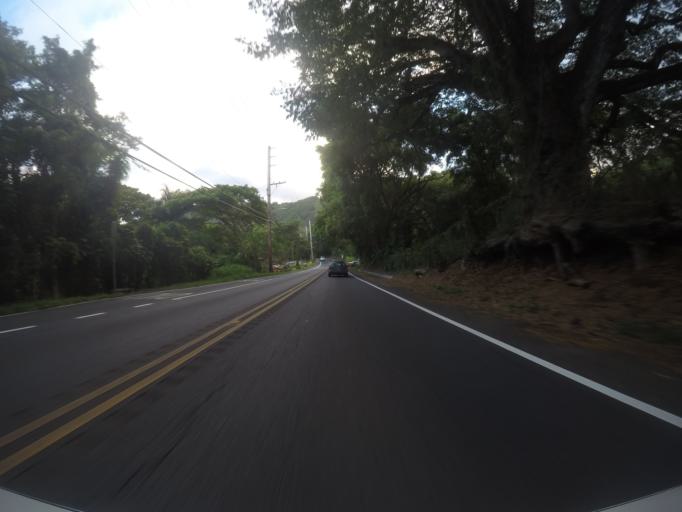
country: US
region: Hawaii
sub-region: Honolulu County
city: Ka'a'awa
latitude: 21.5103
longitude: -157.8532
